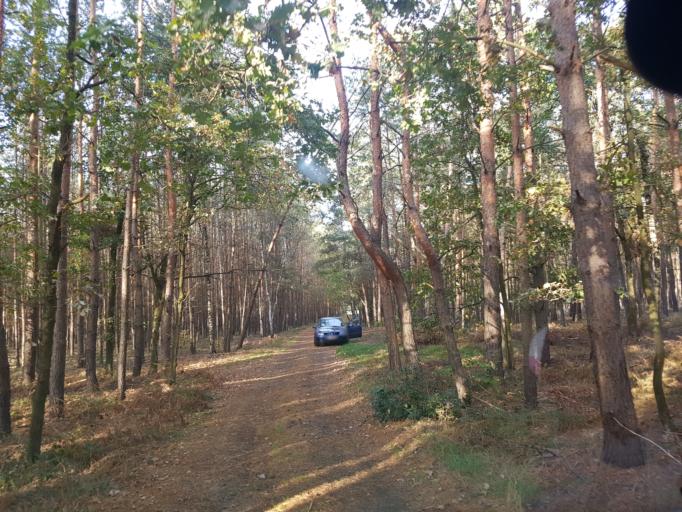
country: DE
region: Brandenburg
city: Bad Liebenwerda
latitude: 51.5429
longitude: 13.3396
